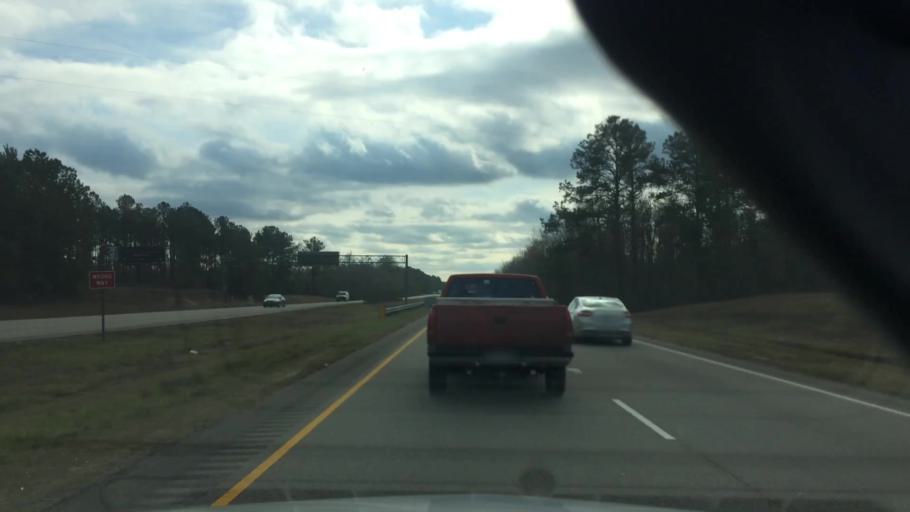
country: US
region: North Carolina
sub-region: Brunswick County
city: Leland
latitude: 34.1643
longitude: -78.0900
